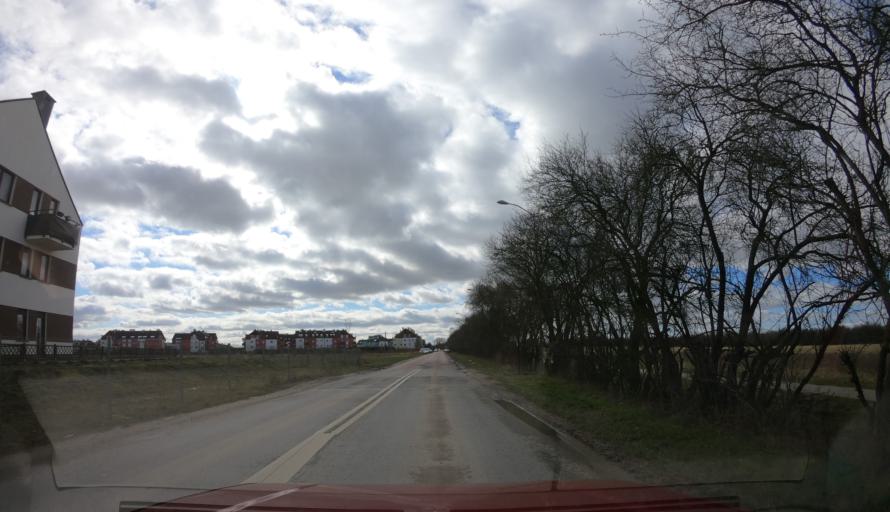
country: PL
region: West Pomeranian Voivodeship
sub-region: Powiat policki
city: Przeclaw
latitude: 53.3916
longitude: 14.4792
